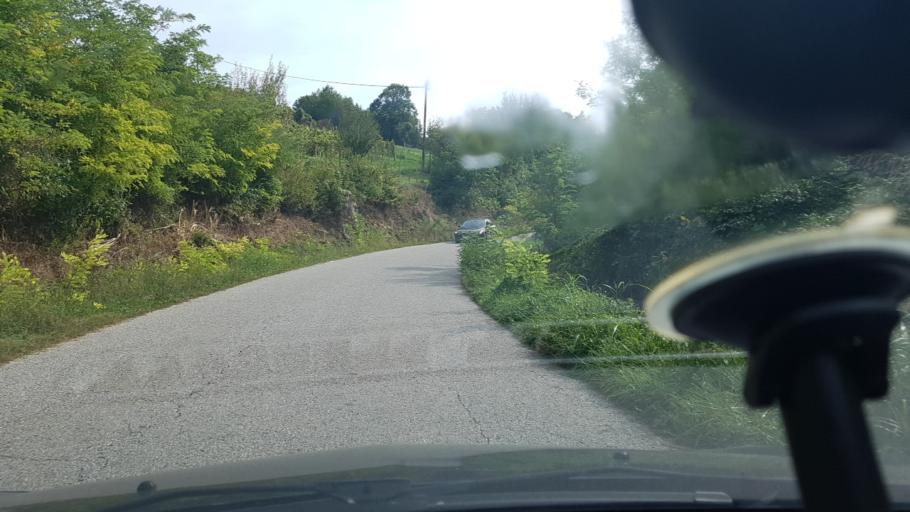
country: HR
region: Varazdinska
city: Ljubescica
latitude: 46.1227
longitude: 16.4404
